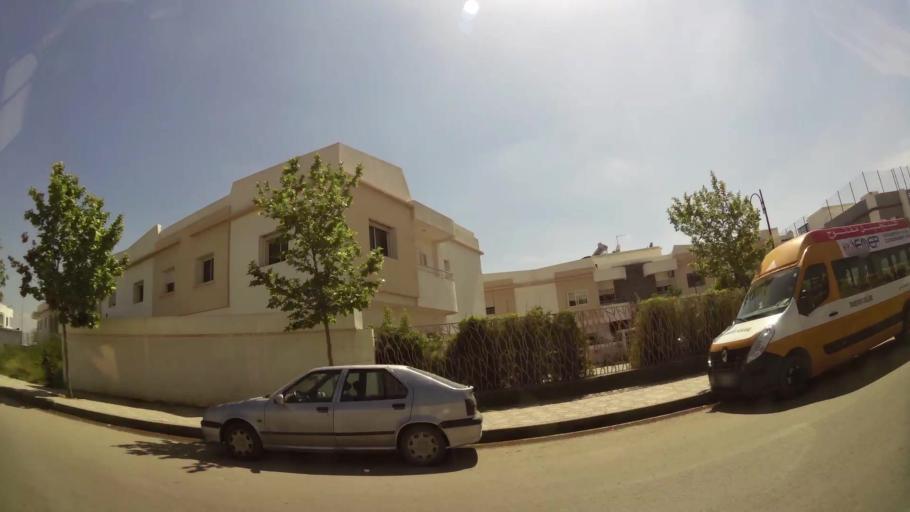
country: MA
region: Fes-Boulemane
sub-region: Fes
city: Fes
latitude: 34.0191
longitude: -5.0227
